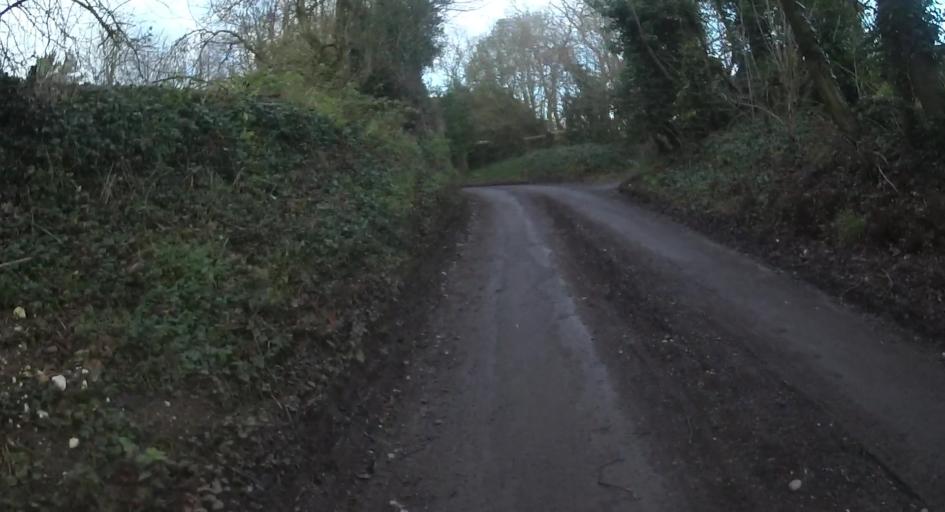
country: GB
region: England
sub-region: Hampshire
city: Tadley
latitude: 51.2877
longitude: -1.1674
